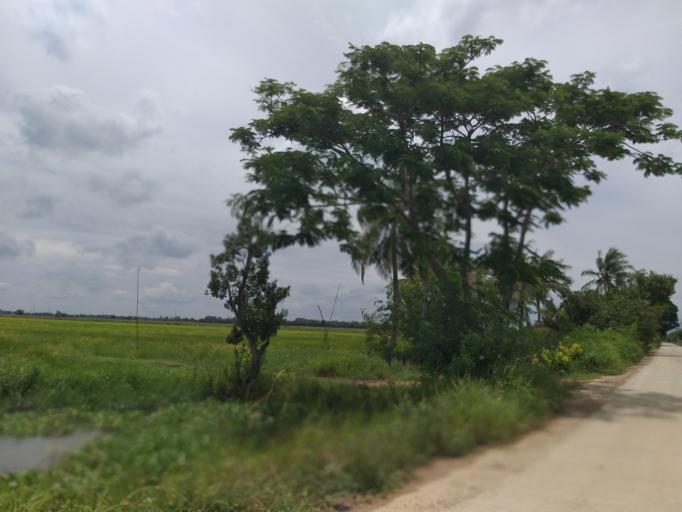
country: TH
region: Pathum Thani
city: Ban Lam Luk Ka
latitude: 14.0234
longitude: 100.8656
